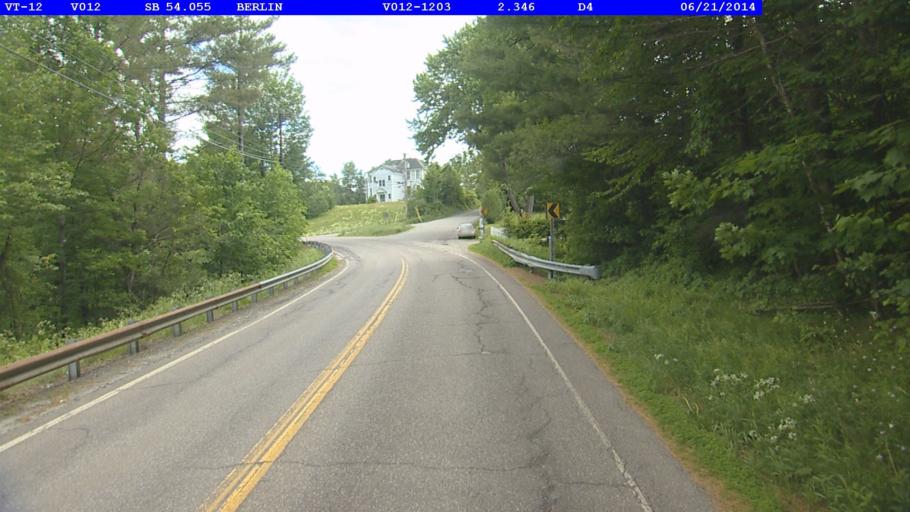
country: US
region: Vermont
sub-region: Washington County
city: Northfield
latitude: 44.2032
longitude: -72.6370
